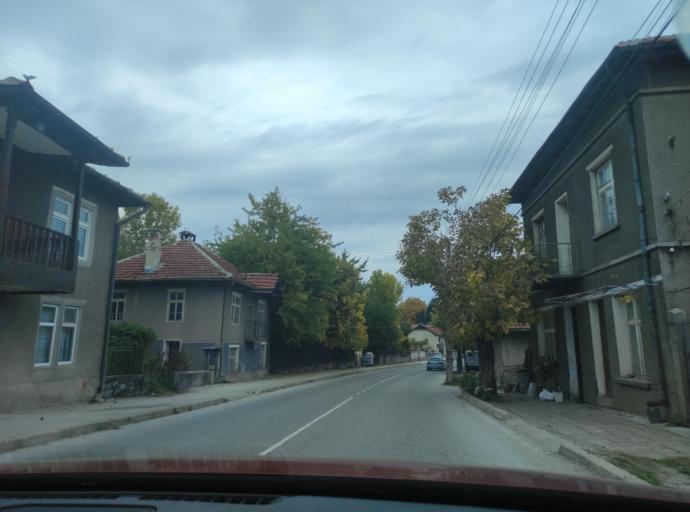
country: BG
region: Montana
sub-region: Obshtina Berkovitsa
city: Berkovitsa
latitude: 43.2017
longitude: 23.1615
